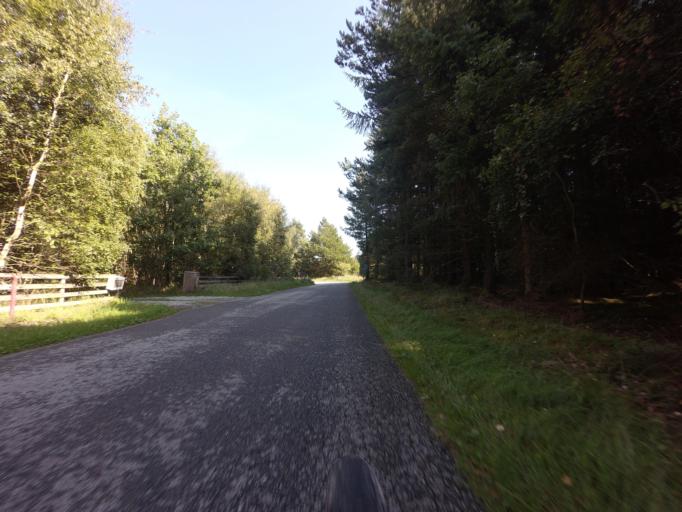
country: DK
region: North Denmark
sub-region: Hjorring Kommune
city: Hirtshals
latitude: 57.5819
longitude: 10.0353
